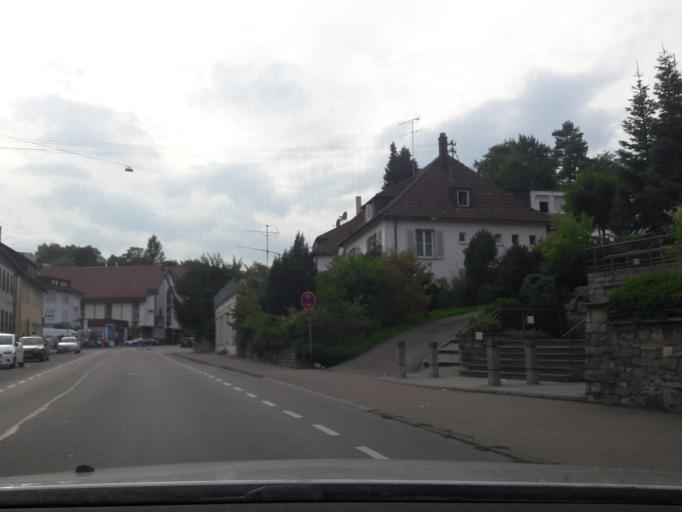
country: DE
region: Baden-Wuerttemberg
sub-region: Regierungsbezirk Stuttgart
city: Backnang
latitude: 48.9506
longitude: 9.4346
